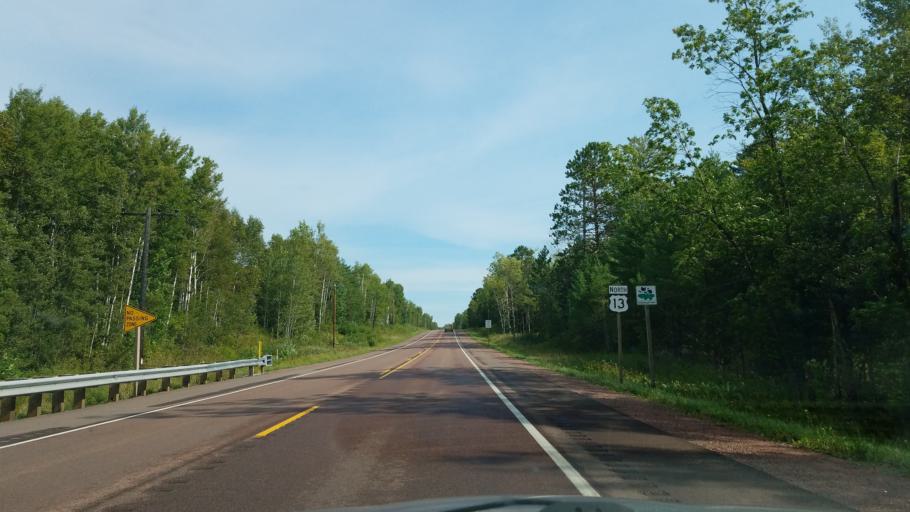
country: US
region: Wisconsin
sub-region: Ashland County
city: Ashland
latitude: 46.6095
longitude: -90.9446
